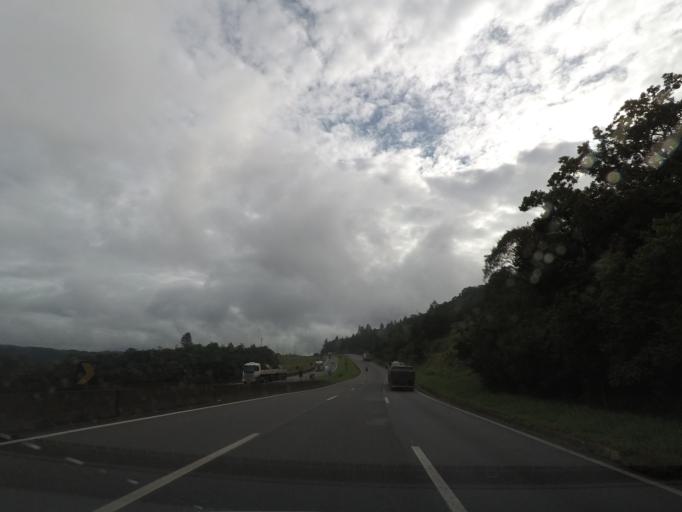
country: BR
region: Parana
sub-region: Campina Grande Do Sul
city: Campina Grande do Sul
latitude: -25.1595
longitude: -48.8619
